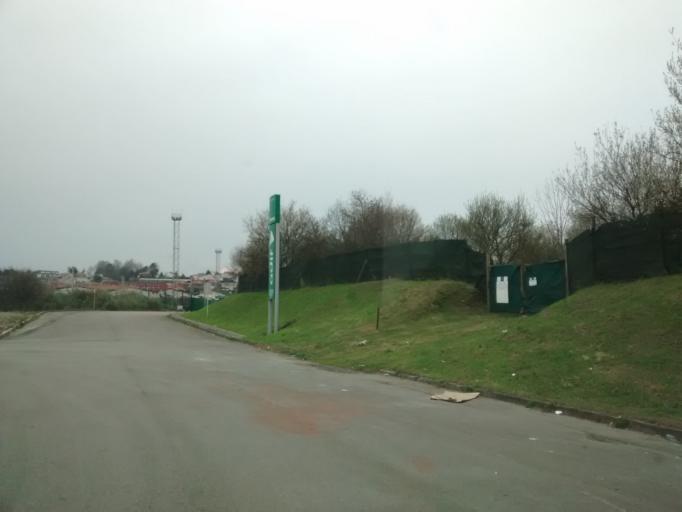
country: ES
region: Cantabria
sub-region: Provincia de Cantabria
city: El Astillero
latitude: 43.4270
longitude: -3.8453
